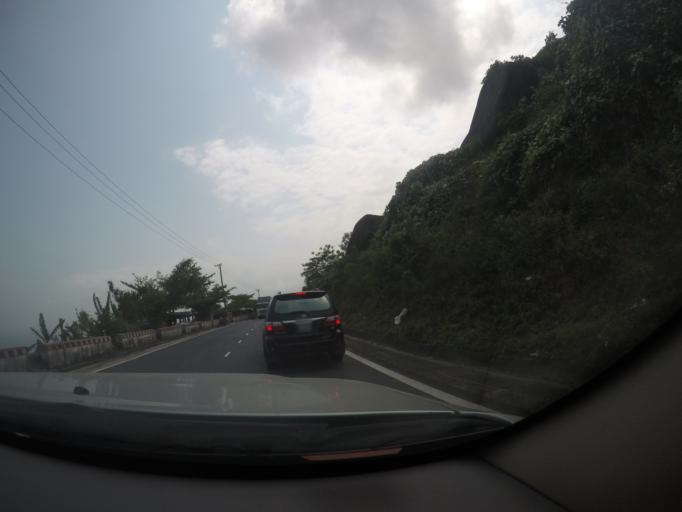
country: VN
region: Da Nang
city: Lien Chieu
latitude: 16.1731
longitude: 108.1300
